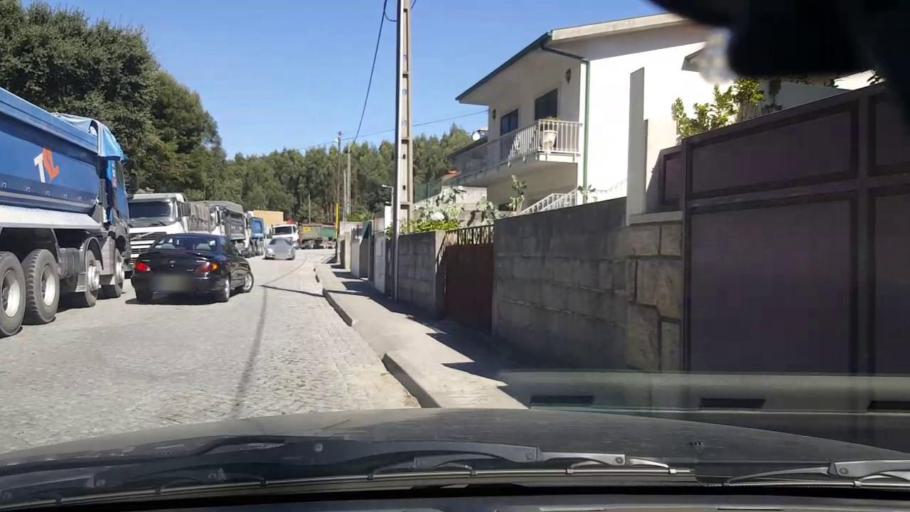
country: PT
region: Porto
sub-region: Maia
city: Gemunde
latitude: 41.3223
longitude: -8.6413
